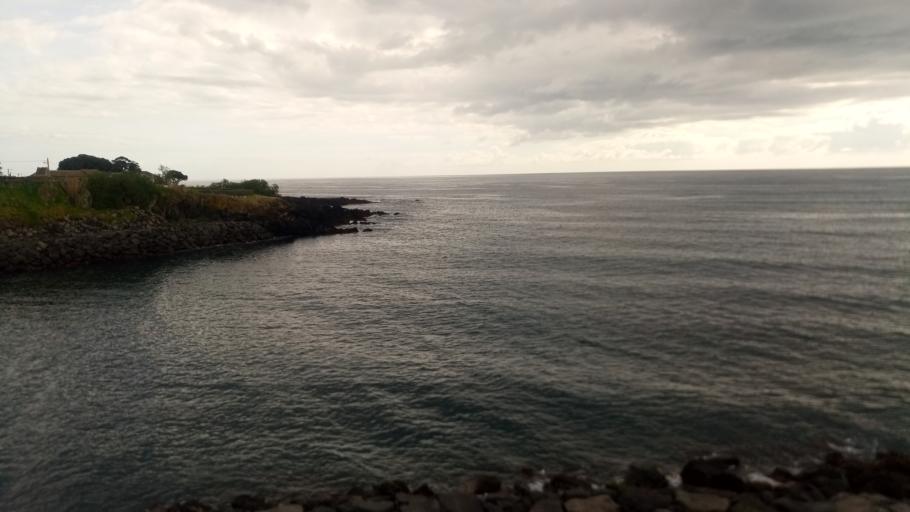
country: PT
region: Azores
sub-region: Praia da Vitoria
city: Praia da Vitoria
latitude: 38.6853
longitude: -27.0560
